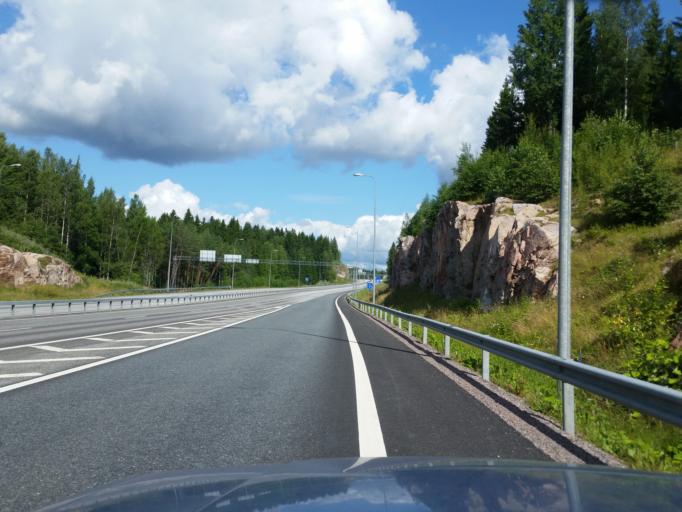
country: FI
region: Uusimaa
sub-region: Helsinki
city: Vihti
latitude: 60.2954
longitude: 24.3649
